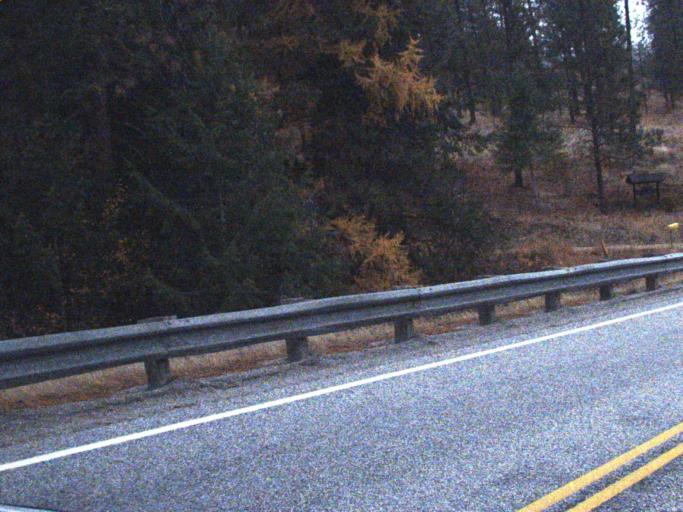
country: US
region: Washington
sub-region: Stevens County
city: Kettle Falls
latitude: 48.7472
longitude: -118.1350
